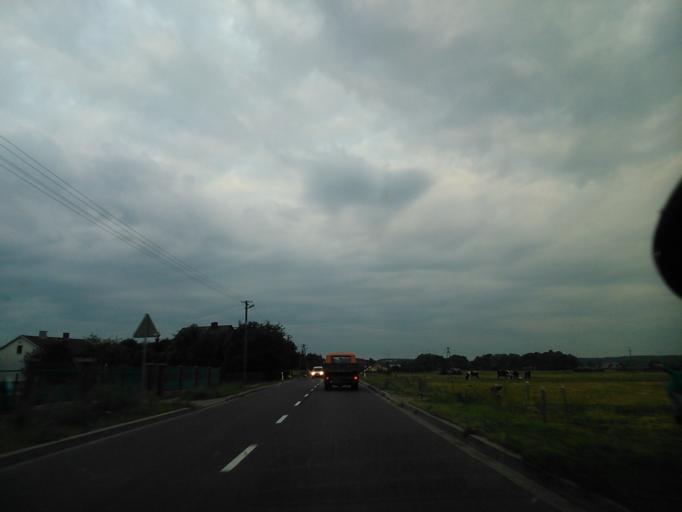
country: PL
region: Masovian Voivodeship
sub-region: Powiat mlawski
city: Lipowiec Koscielny
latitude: 53.1085
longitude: 20.1962
